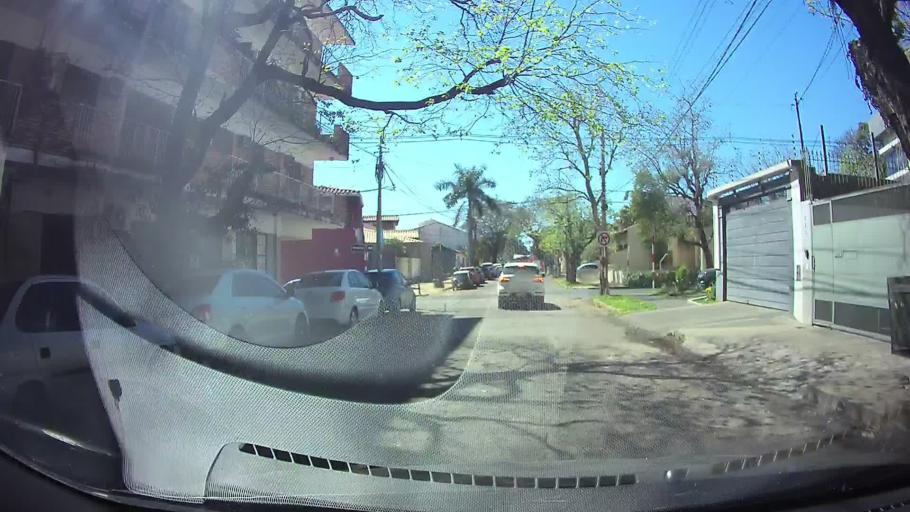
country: PY
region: Asuncion
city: Asuncion
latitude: -25.2833
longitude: -57.6139
